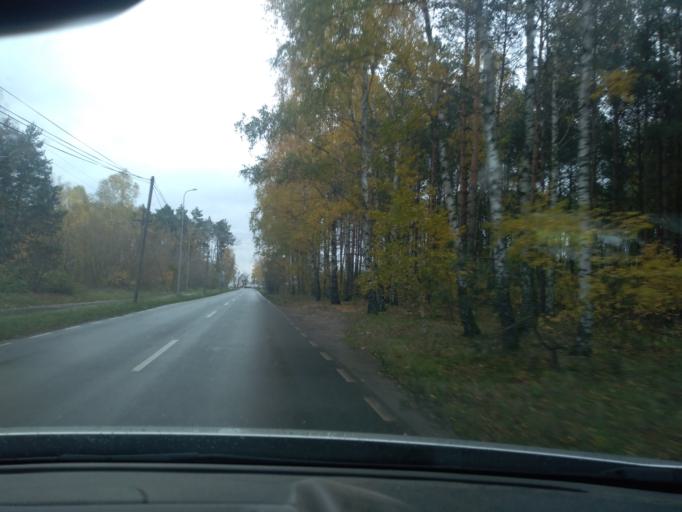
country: PL
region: Greater Poland Voivodeship
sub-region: Powiat obornicki
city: Oborniki
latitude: 52.6456
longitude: 16.8448
